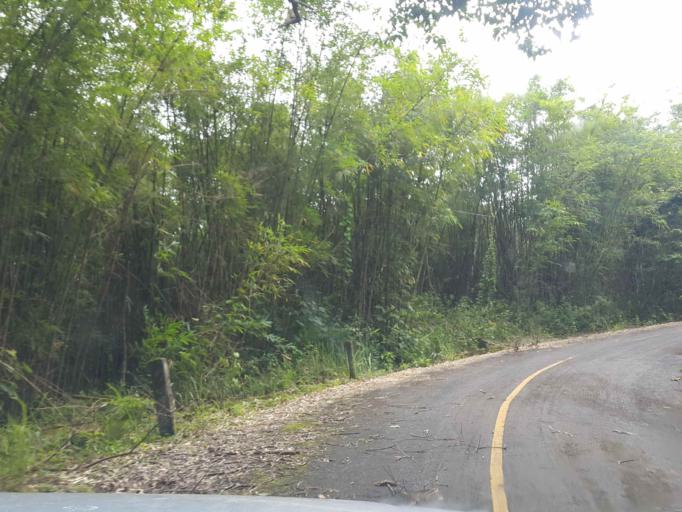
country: TH
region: Tak
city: Tak
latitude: 16.7920
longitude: 98.9234
